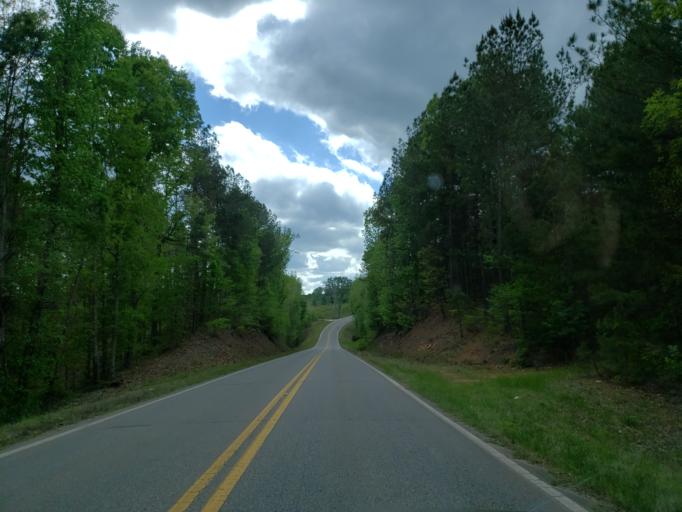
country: US
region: Georgia
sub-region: Haralson County
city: Tallapoosa
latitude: 33.7456
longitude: -85.3820
